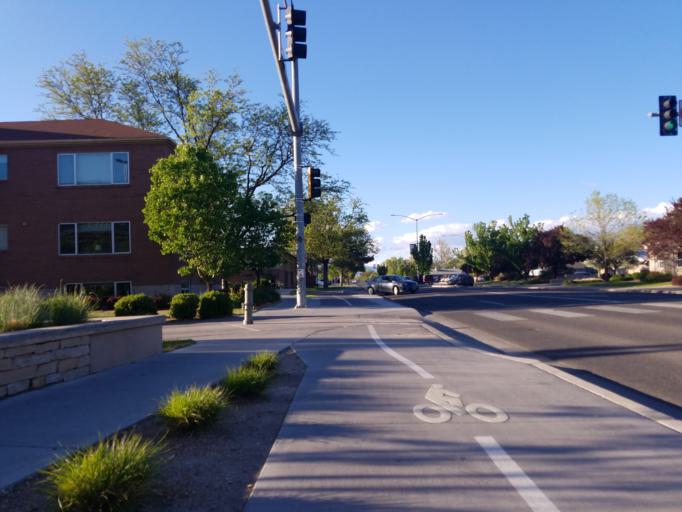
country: US
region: Colorado
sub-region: Mesa County
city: Grand Junction
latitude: 39.0809
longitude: -108.5525
